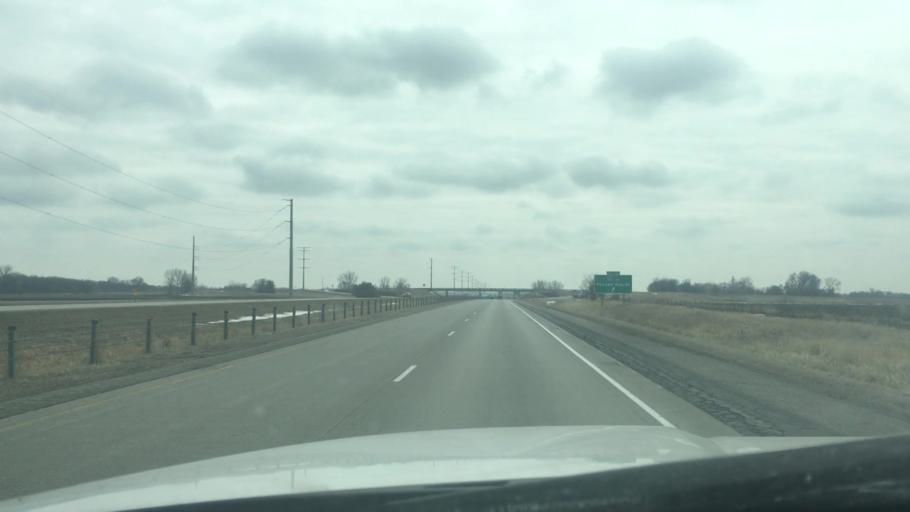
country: US
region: Minnesota
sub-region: Clay County
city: Barnesville
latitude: 46.5641
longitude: -96.3205
